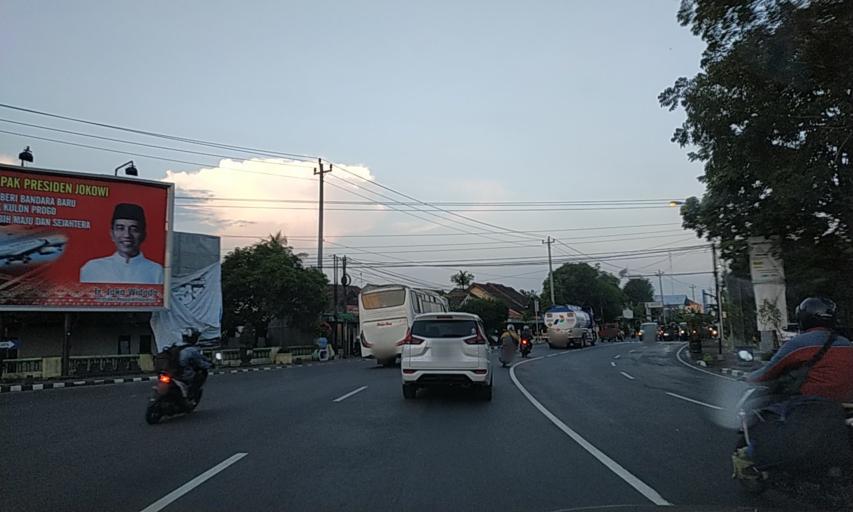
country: ID
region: Daerah Istimewa Yogyakarta
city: Srandakan
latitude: -7.8647
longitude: 110.1517
